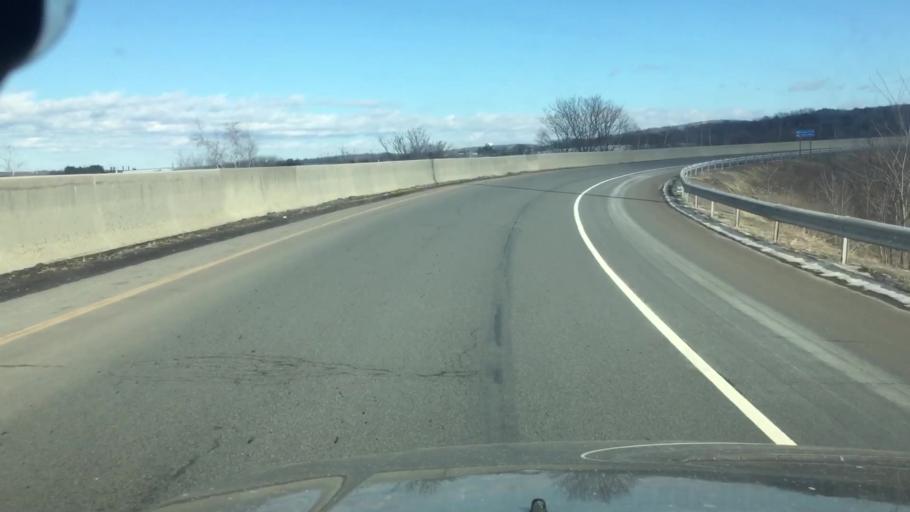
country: US
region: Pennsylvania
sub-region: Luzerne County
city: Hudson
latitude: 41.2535
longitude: -75.8356
